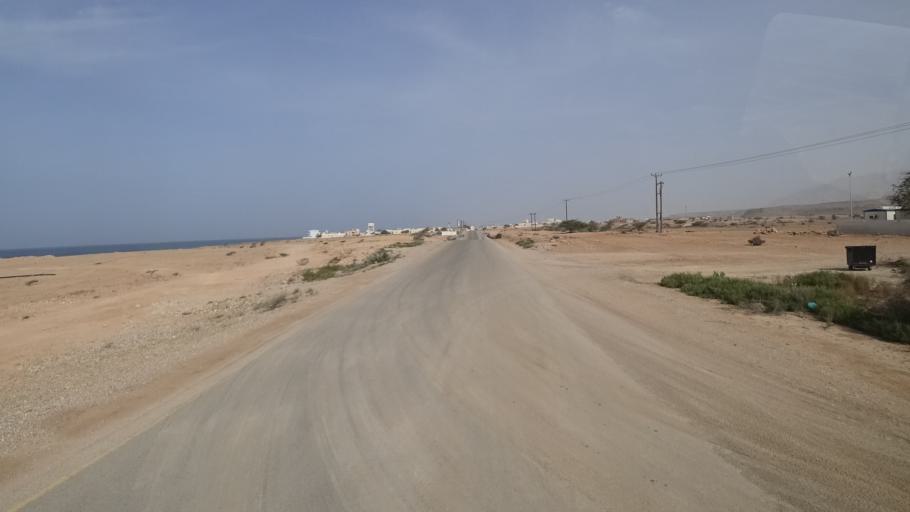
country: OM
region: Ash Sharqiyah
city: Sur
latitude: 22.9953
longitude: 59.1296
